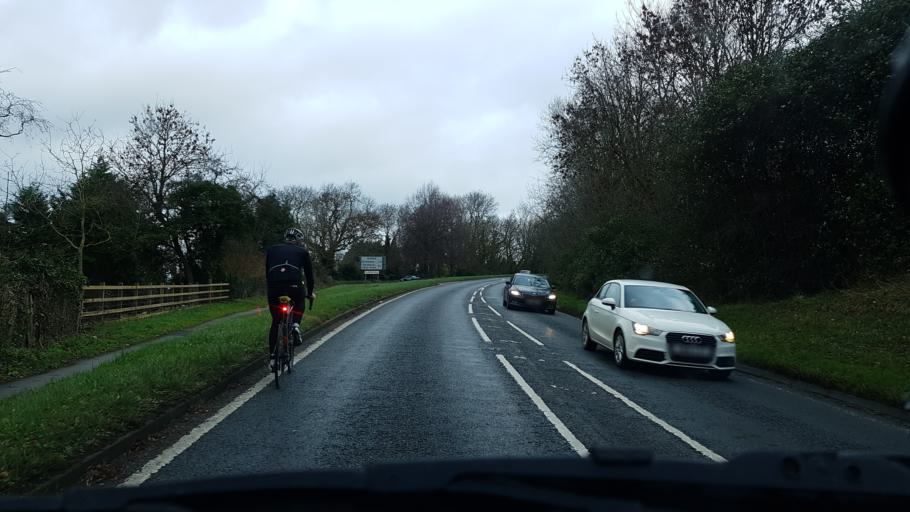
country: GB
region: England
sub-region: Gloucestershire
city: Gotherington
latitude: 51.9313
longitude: -2.0398
